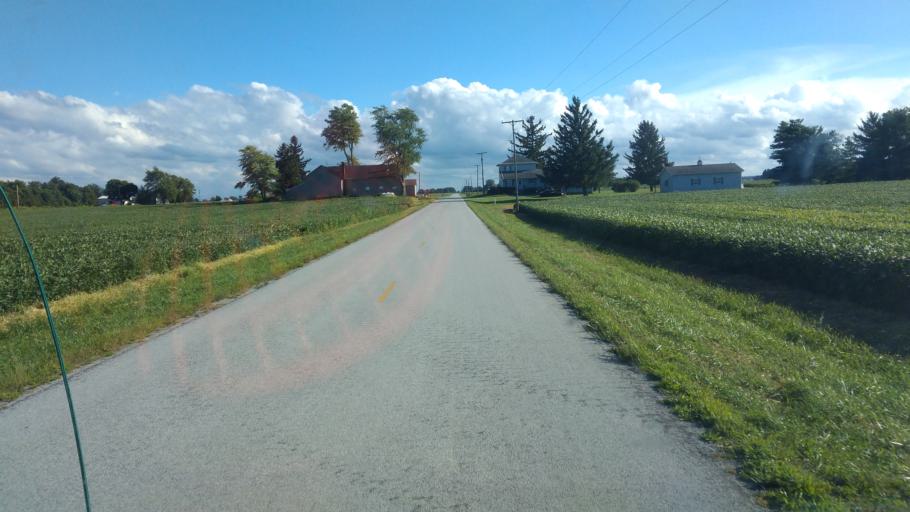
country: US
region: Ohio
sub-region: Hardin County
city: Ada
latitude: 40.7635
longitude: -83.6904
